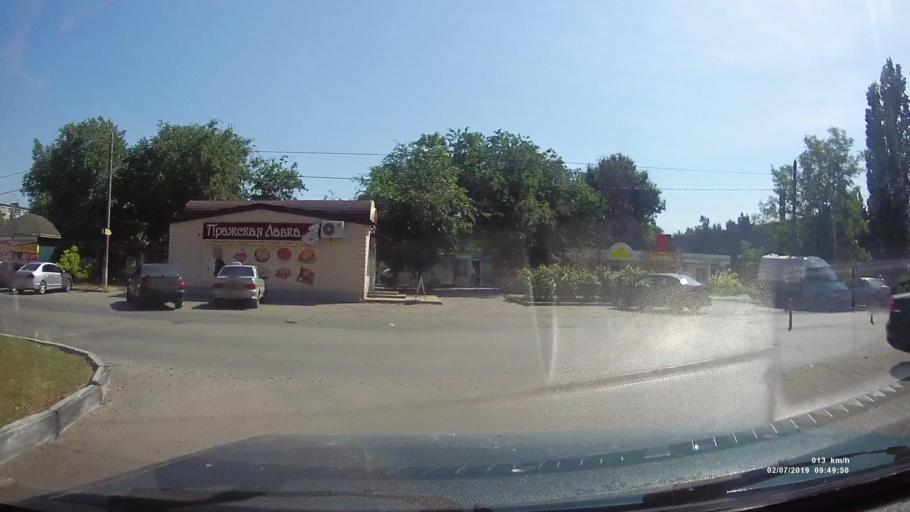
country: RU
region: Rostov
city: Azov
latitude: 47.1033
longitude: 39.4025
